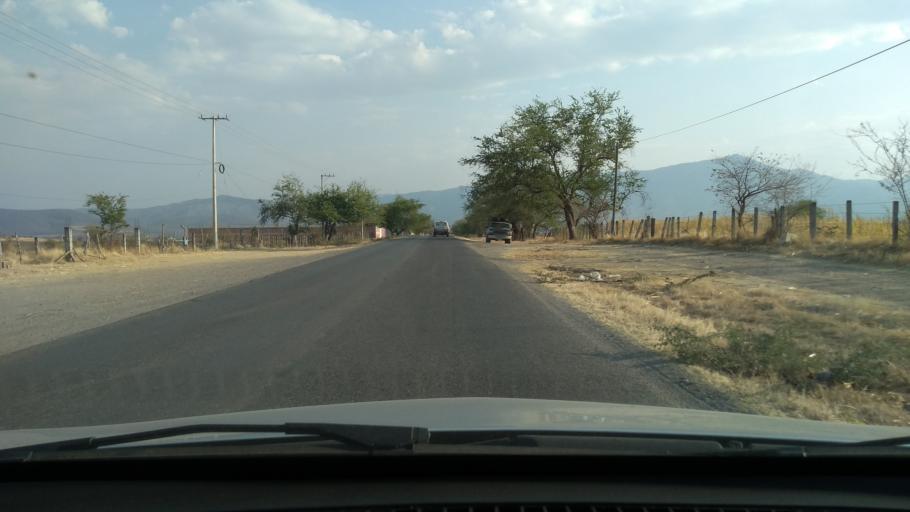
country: MX
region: Morelos
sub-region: Jojutla
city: Tehuixtla
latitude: 18.5837
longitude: -99.2642
